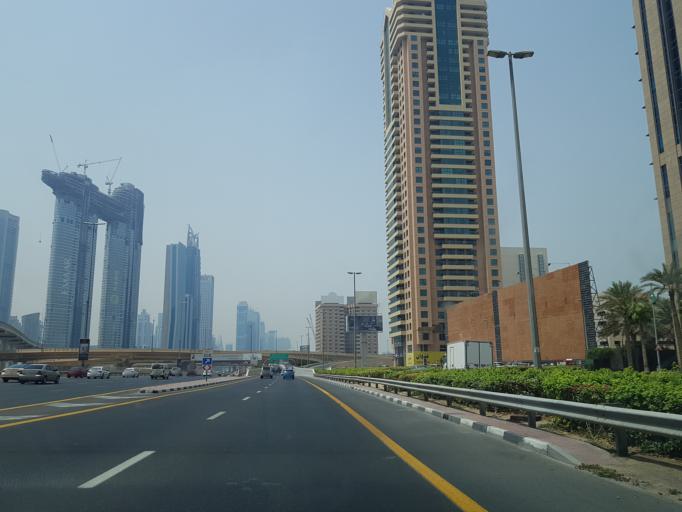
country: AE
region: Dubai
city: Dubai
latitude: 25.2080
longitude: 55.2726
